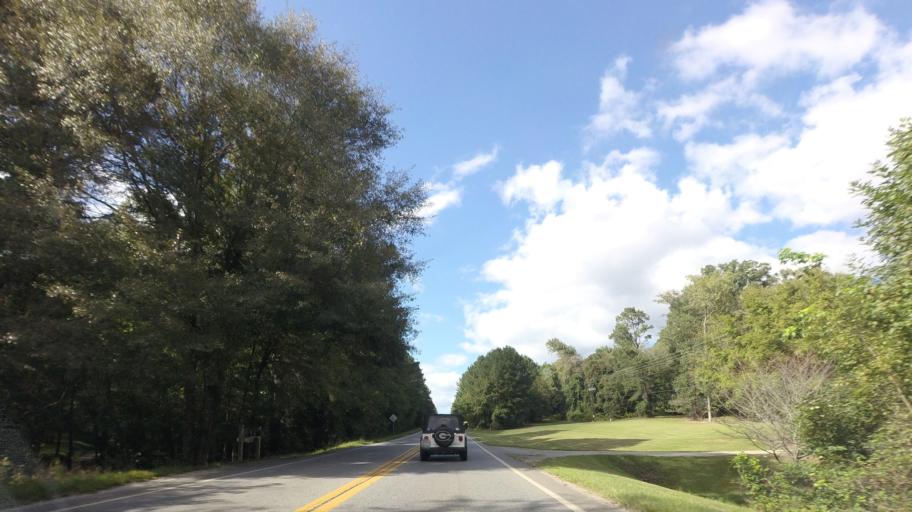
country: US
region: Georgia
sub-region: Bibb County
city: Macon
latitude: 32.9779
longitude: -83.7303
